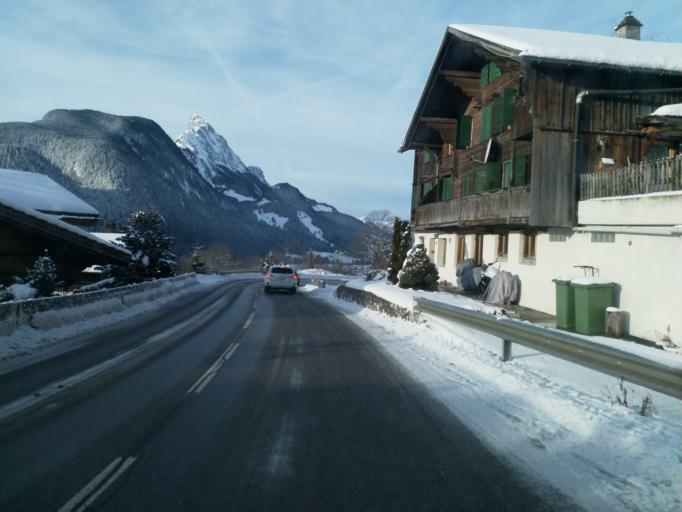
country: CH
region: Bern
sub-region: Obersimmental-Saanen District
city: Saanen
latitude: 46.4932
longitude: 7.2693
